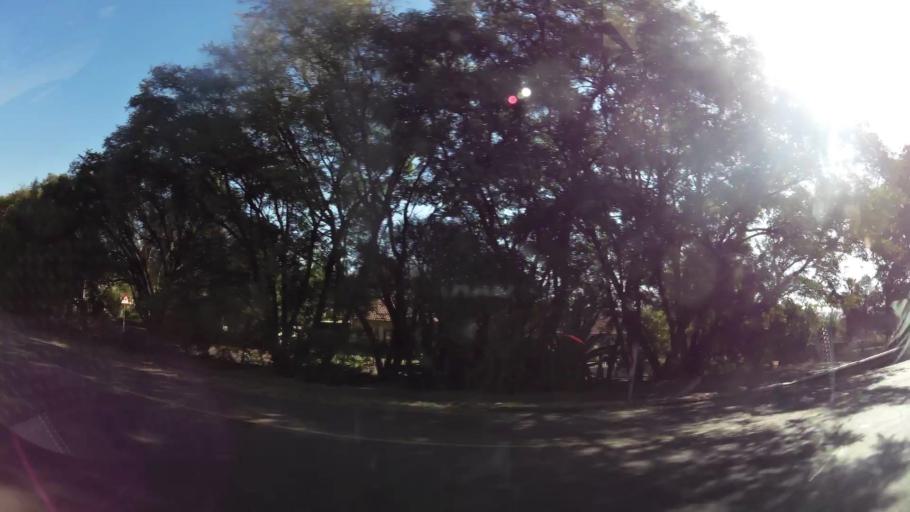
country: ZA
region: Gauteng
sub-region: City of Tshwane Metropolitan Municipality
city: Pretoria
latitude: -25.7255
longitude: 28.2582
